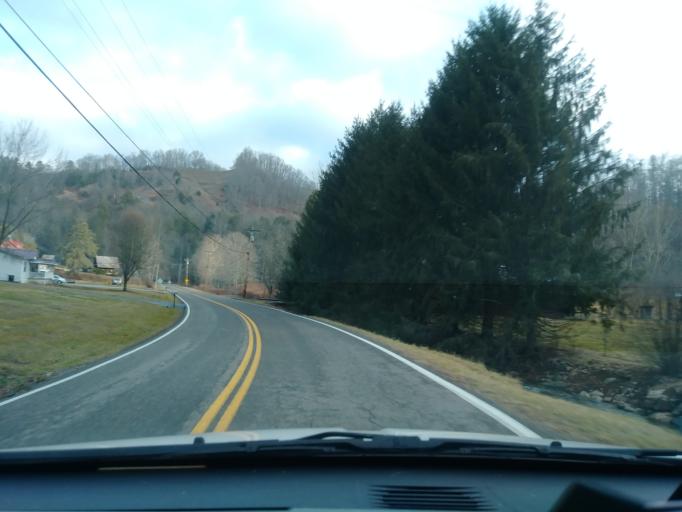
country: US
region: Tennessee
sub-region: Carter County
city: Roan Mountain
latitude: 36.2181
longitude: -82.1990
